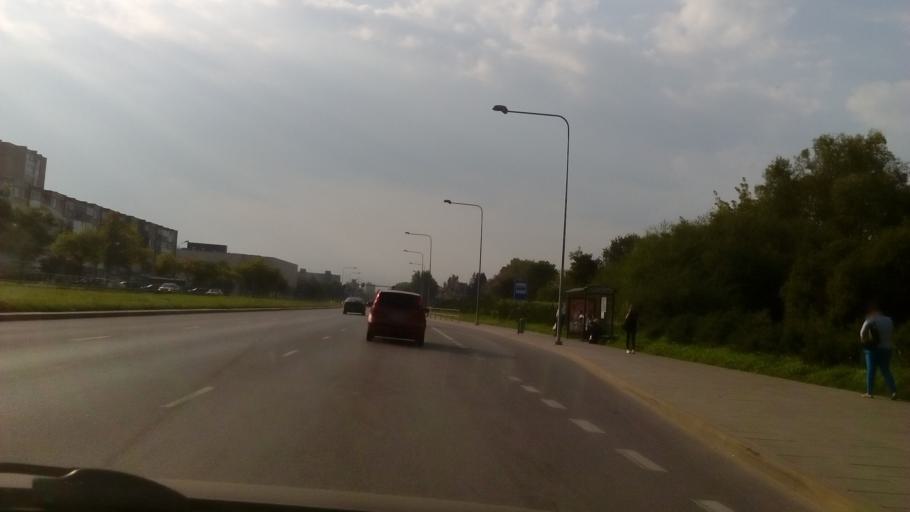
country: LT
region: Alytaus apskritis
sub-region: Alytus
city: Alytus
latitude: 54.4068
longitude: 24.0183
